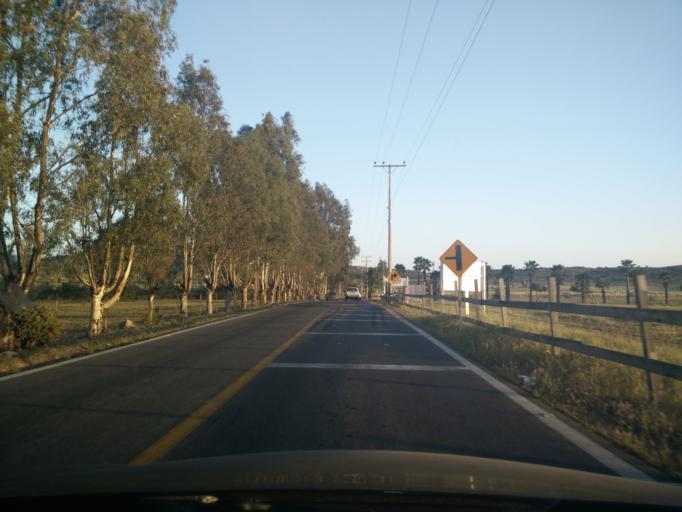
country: MX
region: Baja California
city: El Sauzal
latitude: 32.0146
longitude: -116.6729
